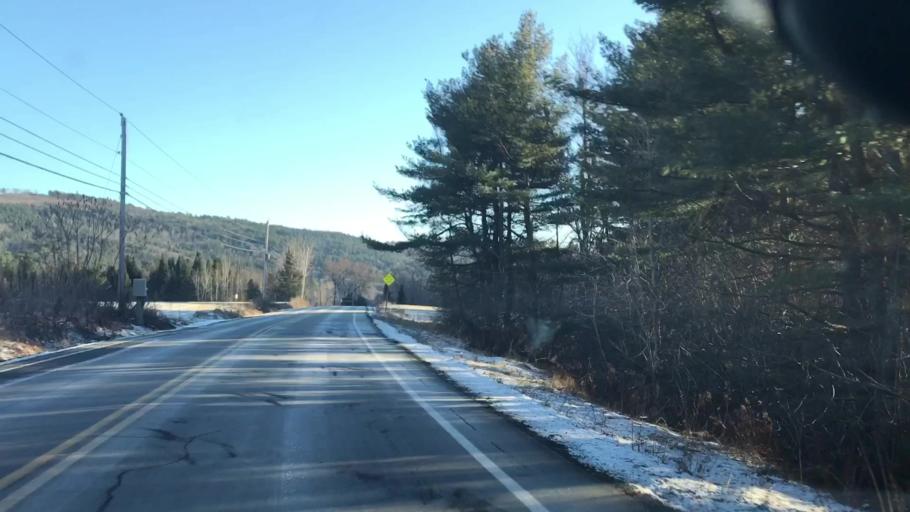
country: US
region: New Hampshire
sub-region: Grafton County
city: Lyme Town Offices
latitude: 43.8381
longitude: -72.1499
